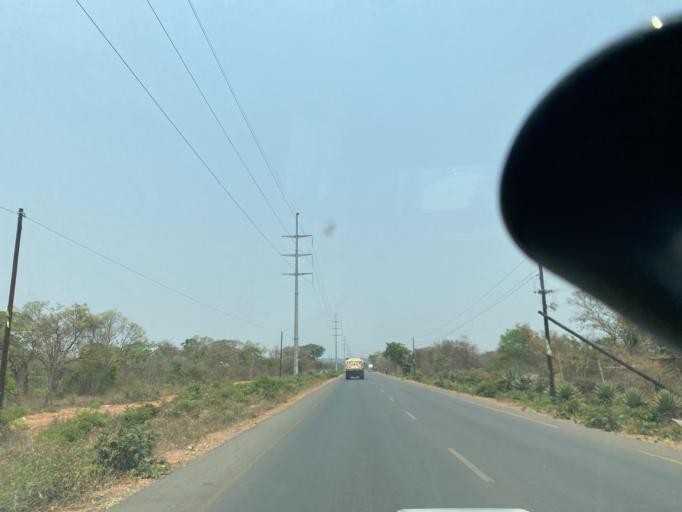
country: ZM
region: Lusaka
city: Lusaka
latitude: -15.5148
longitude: 28.4529
